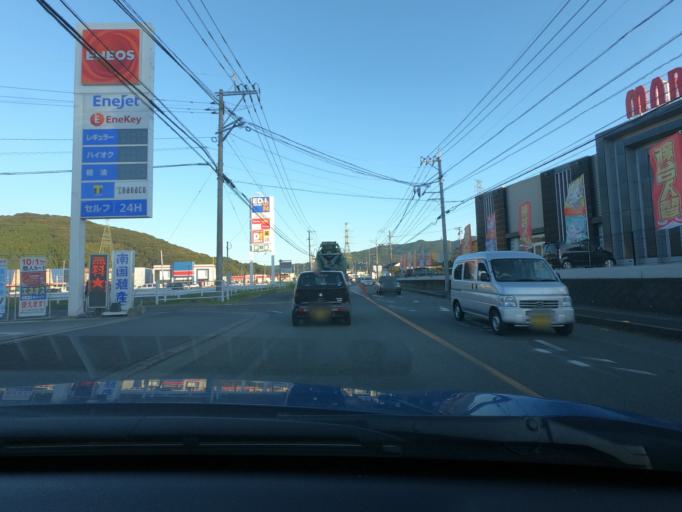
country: JP
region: Kagoshima
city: Satsumasendai
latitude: 31.8087
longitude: 130.3362
